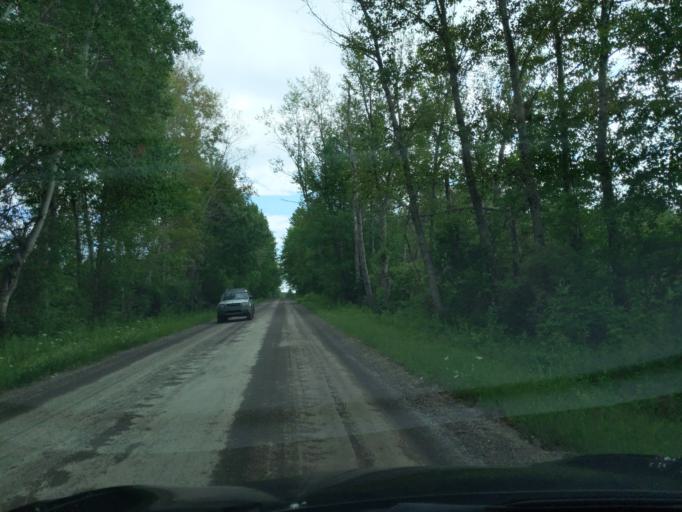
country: US
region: Michigan
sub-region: Clare County
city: Harrison
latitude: 43.9813
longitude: -84.9983
